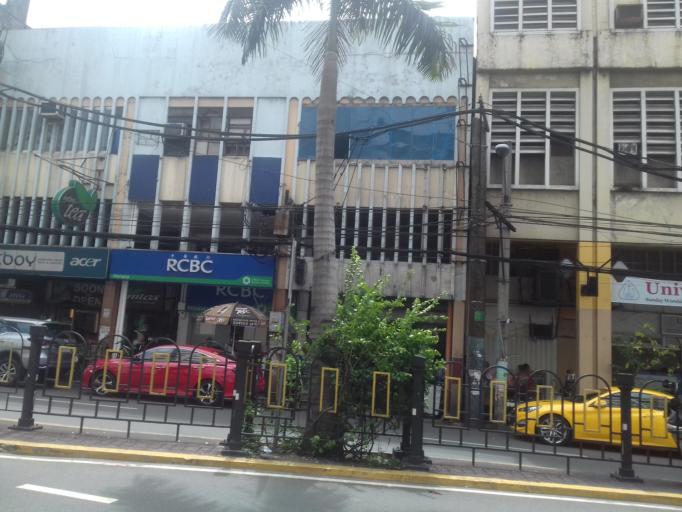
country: PH
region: Metro Manila
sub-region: City of Manila
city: Quiapo
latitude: 14.6029
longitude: 120.9870
